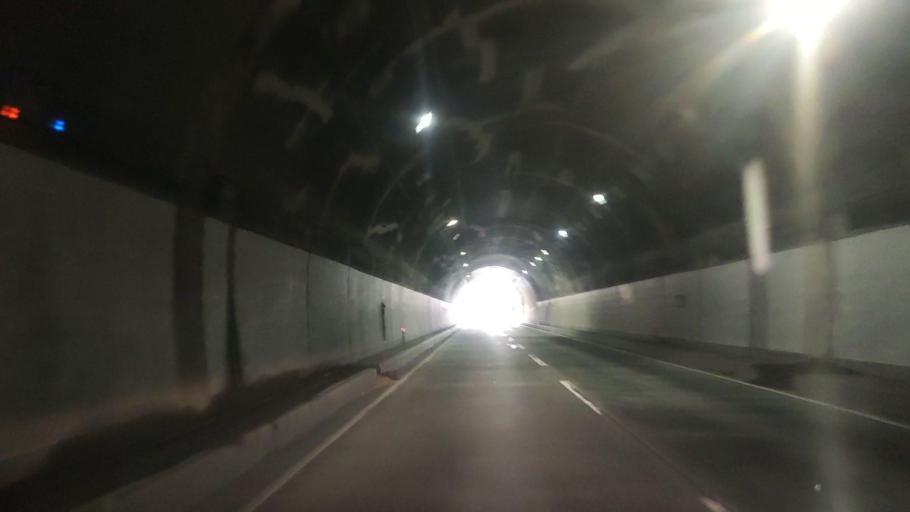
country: JP
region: Kagoshima
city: Okuchi-shinohara
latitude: 31.9719
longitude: 130.7407
